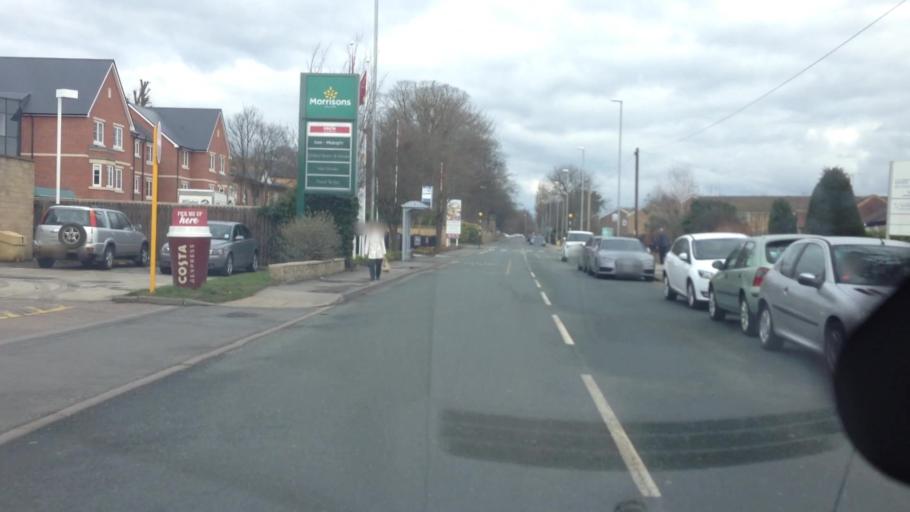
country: GB
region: England
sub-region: City and Borough of Leeds
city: Wetherby
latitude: 53.9318
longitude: -1.3831
